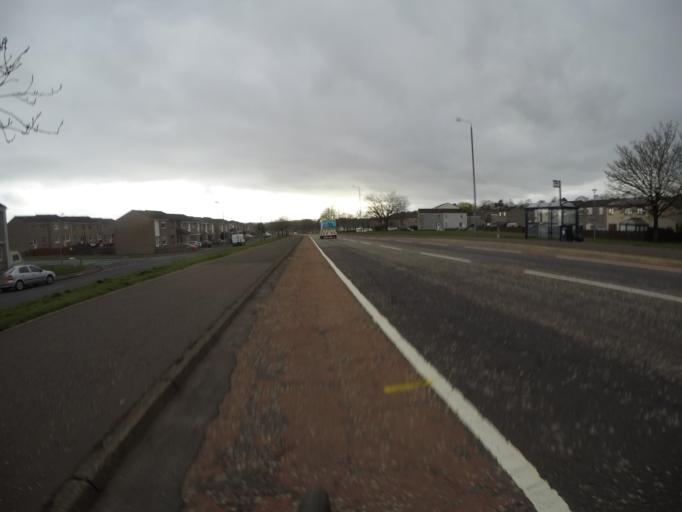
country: GB
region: Scotland
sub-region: East Ayrshire
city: Kilmarnock
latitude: 55.6204
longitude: -4.4737
